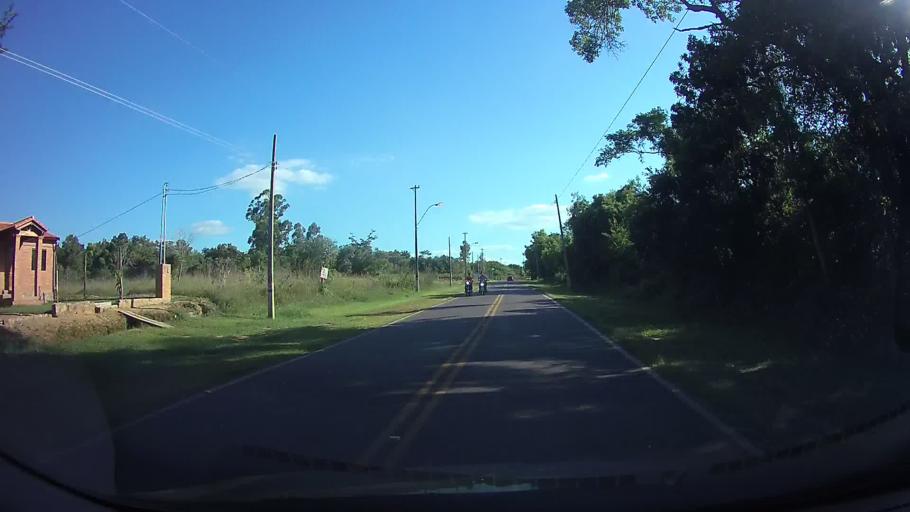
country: PY
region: Cordillera
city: Atyra
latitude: -25.3043
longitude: -57.1868
